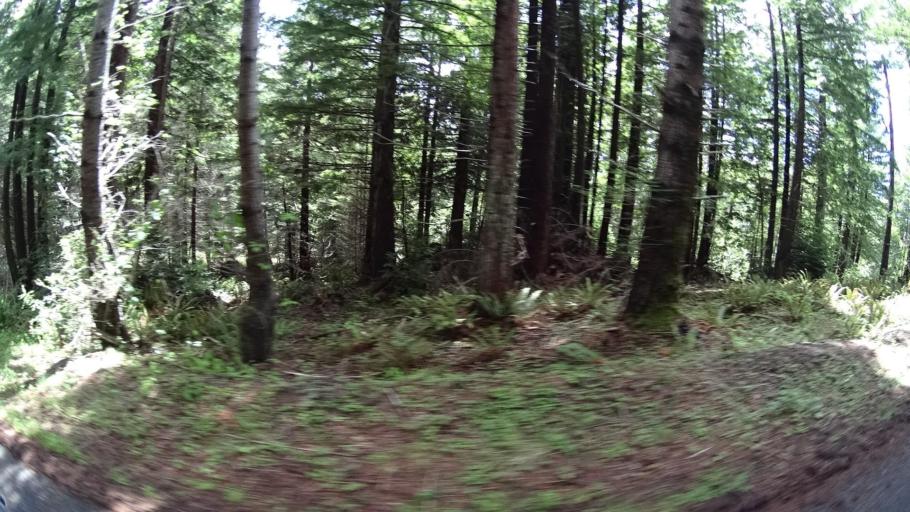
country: US
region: California
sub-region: Humboldt County
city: Blue Lake
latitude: 40.8443
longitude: -123.9216
